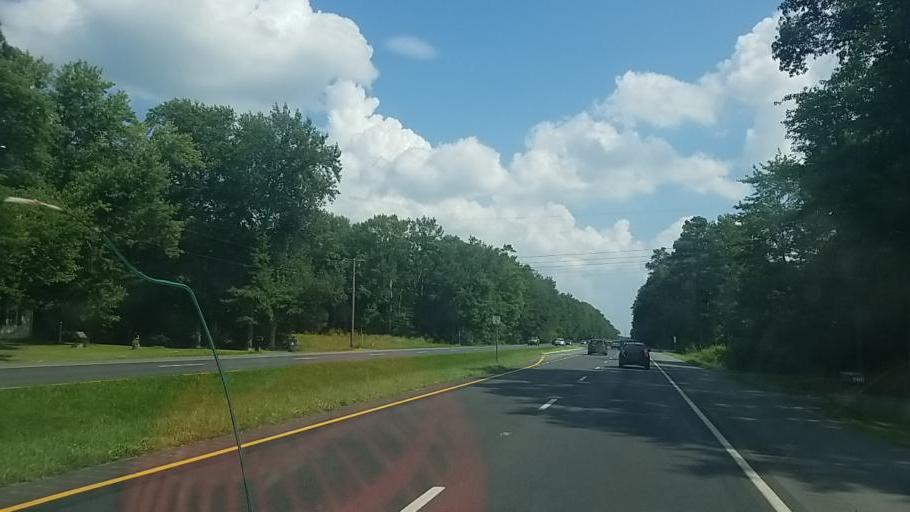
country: US
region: Delaware
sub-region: Sussex County
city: Millsboro
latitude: 38.5598
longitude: -75.2730
